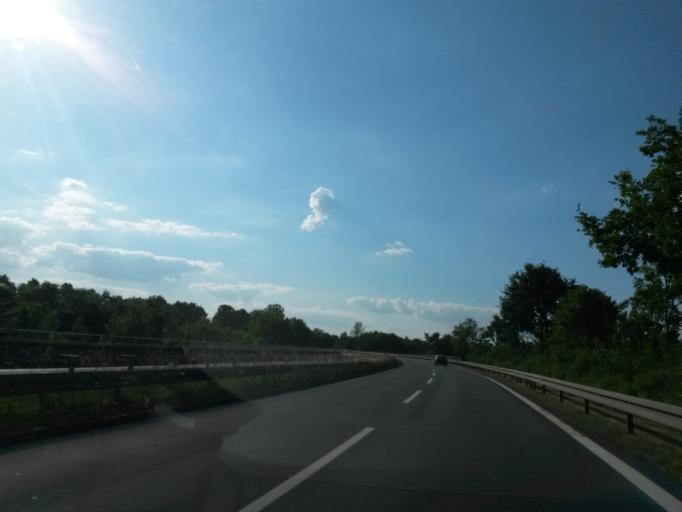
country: DE
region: Bavaria
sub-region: Regierungsbezirk Mittelfranken
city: Zirndorf
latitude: 49.4752
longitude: 10.9465
